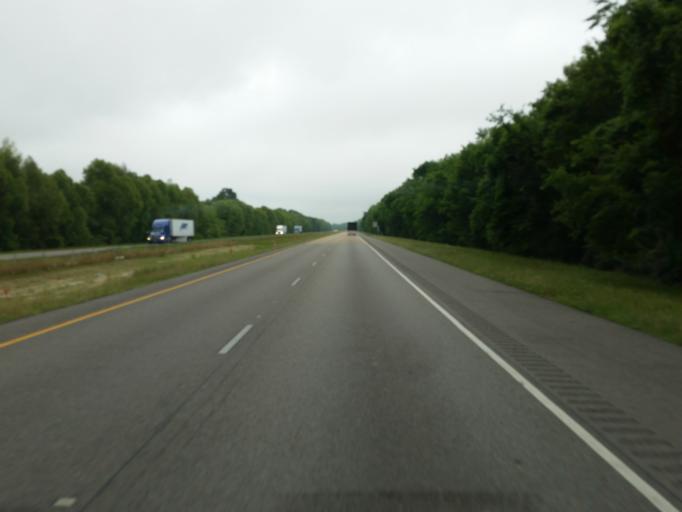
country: US
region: Louisiana
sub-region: Madison Parish
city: Tallulah
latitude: 32.3457
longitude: -91.0812
